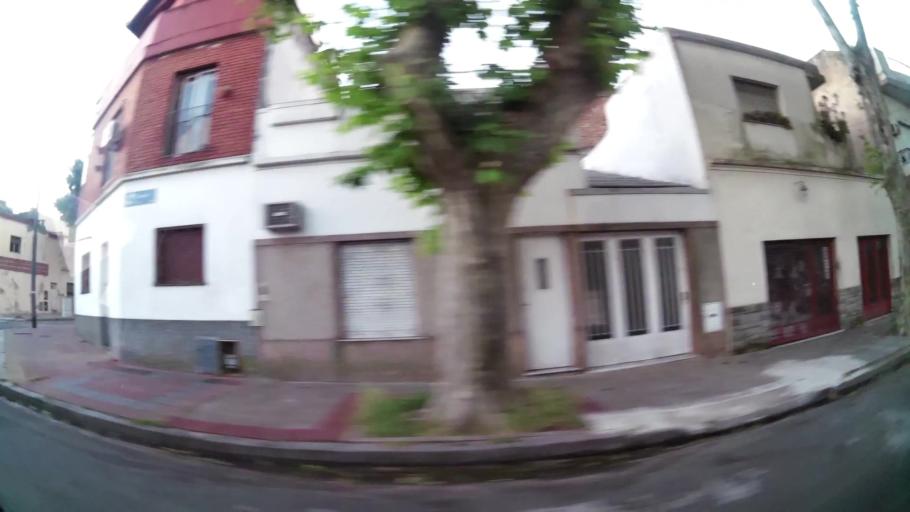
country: AR
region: Buenos Aires F.D.
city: Villa Lugano
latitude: -34.6412
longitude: -58.4411
